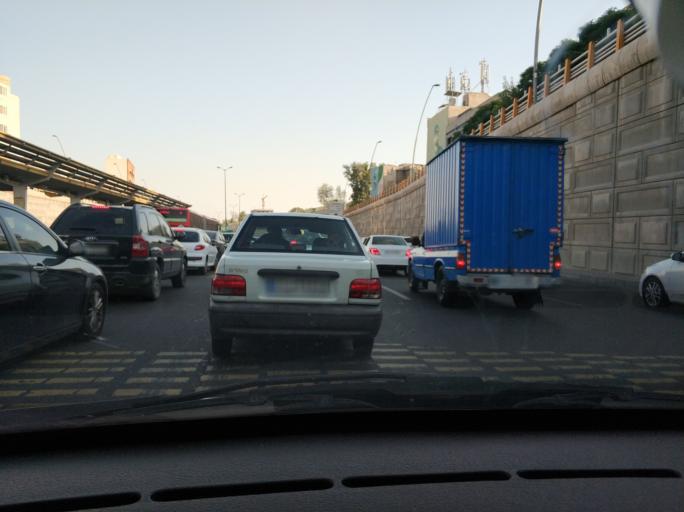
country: IR
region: Tehran
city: Tehran
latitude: 35.6968
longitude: 51.4567
